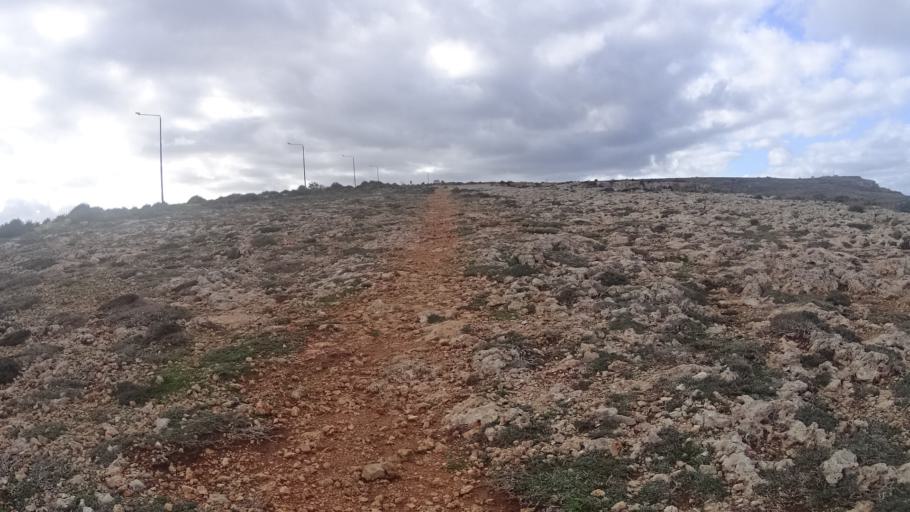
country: MT
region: Il-Mellieha
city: Mellieha
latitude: 35.9839
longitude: 14.3347
